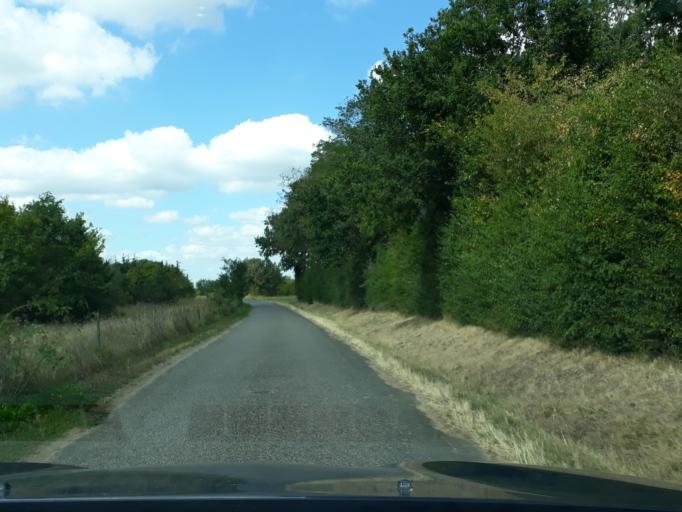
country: FR
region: Centre
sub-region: Departement du Loiret
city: Saint-Cyr-en-Val
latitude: 47.8520
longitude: 1.9812
